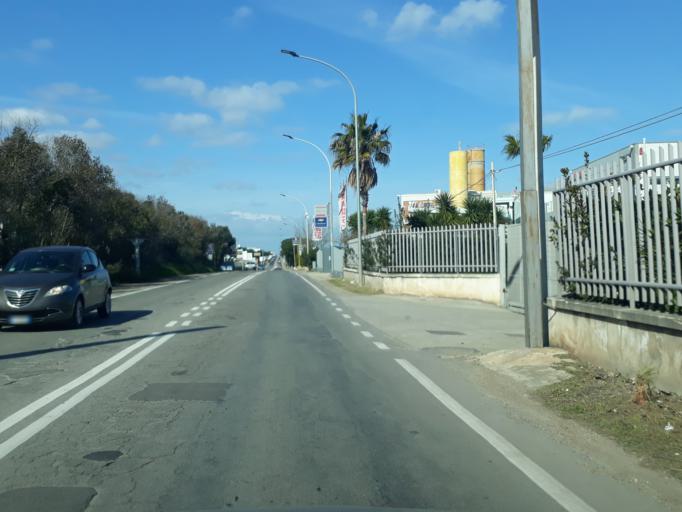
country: IT
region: Apulia
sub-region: Provincia di Bari
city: Monopoli
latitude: 40.9642
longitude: 17.2767
